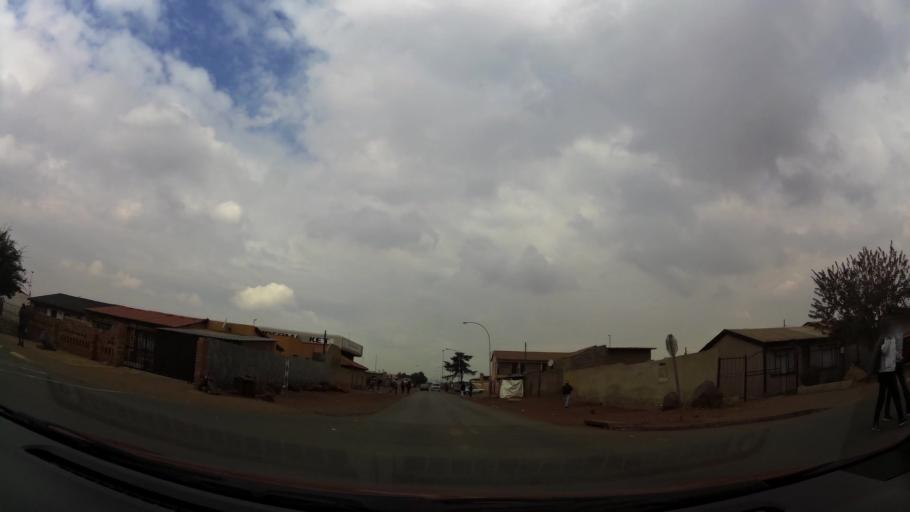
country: ZA
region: Gauteng
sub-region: City of Johannesburg Metropolitan Municipality
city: Soweto
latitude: -26.2584
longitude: 27.8324
